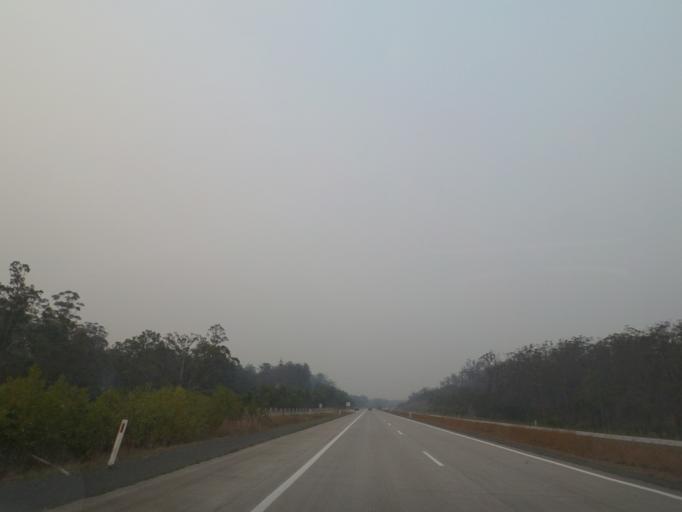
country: AU
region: New South Wales
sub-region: Kempsey
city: Kempsey
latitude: -31.1184
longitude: 152.8306
